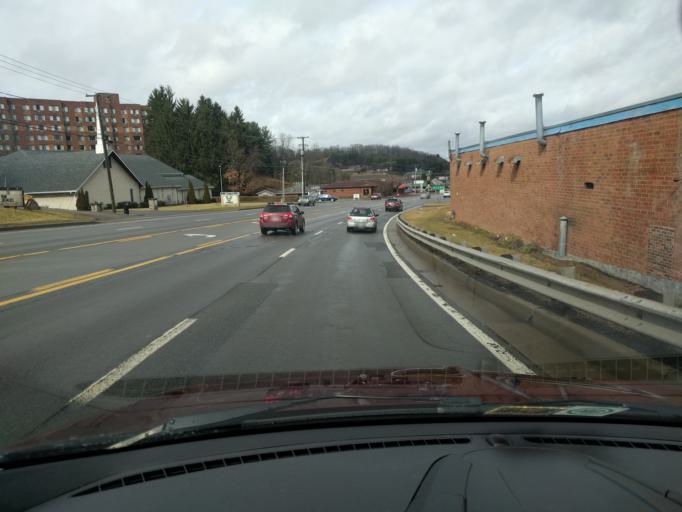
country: US
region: West Virginia
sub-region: Raleigh County
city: Beckley
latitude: 37.7975
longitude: -81.1843
